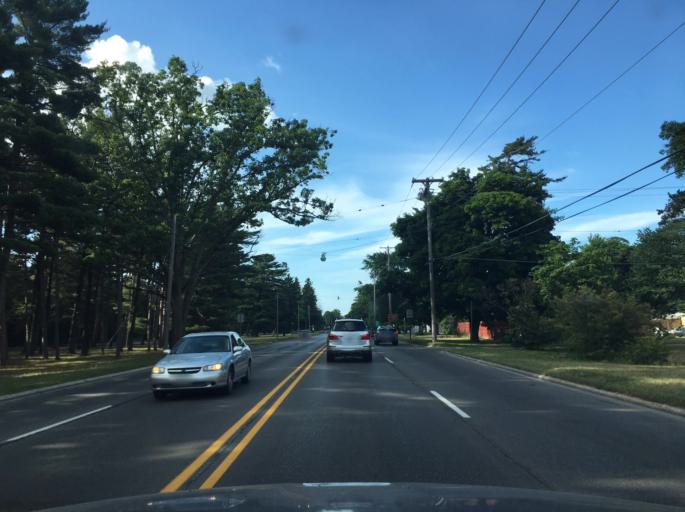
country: US
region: Michigan
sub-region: Grand Traverse County
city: Traverse City
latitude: 44.7536
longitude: -85.6349
